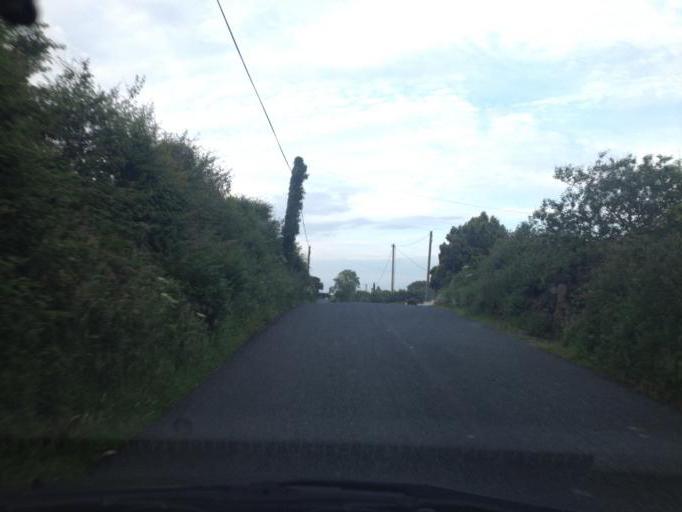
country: IE
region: Connaught
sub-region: Sligo
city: Strandhill
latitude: 54.3875
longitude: -8.5494
